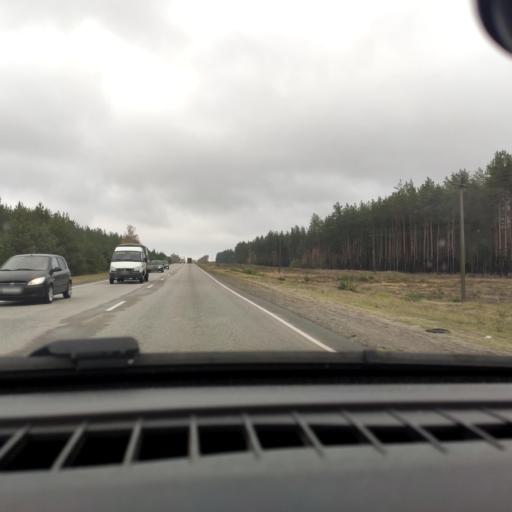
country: RU
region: Voronezj
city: Uryv-Pokrovka
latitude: 51.0526
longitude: 38.9863
